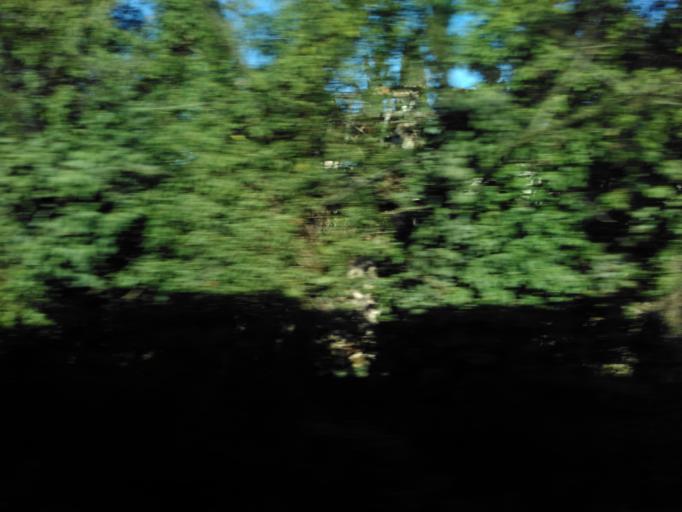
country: IT
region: Veneto
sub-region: Provincia di Verona
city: Montorio
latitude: 45.4251
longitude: 11.0596
